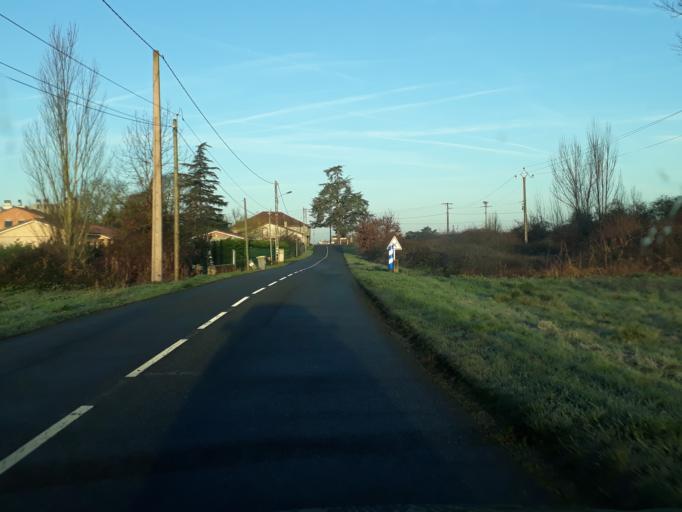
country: FR
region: Midi-Pyrenees
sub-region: Departement de la Haute-Garonne
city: Marquefave
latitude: 43.3192
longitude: 1.2358
